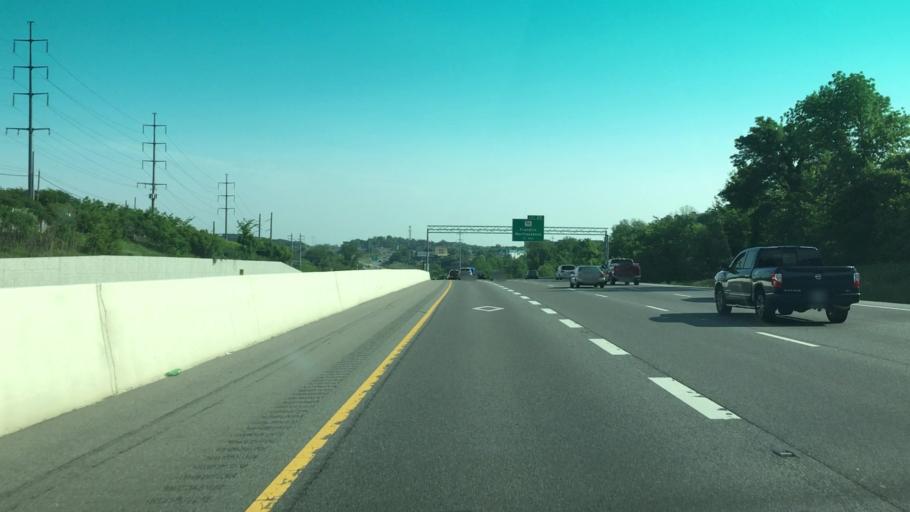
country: US
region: Tennessee
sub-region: Williamson County
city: Franklin
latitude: 35.9025
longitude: -86.8265
